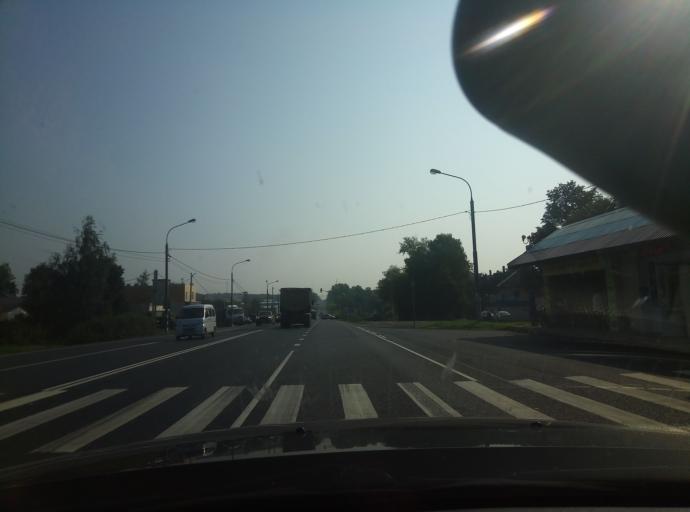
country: RU
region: Kaluga
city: Belousovo
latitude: 55.0915
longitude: 36.6629
